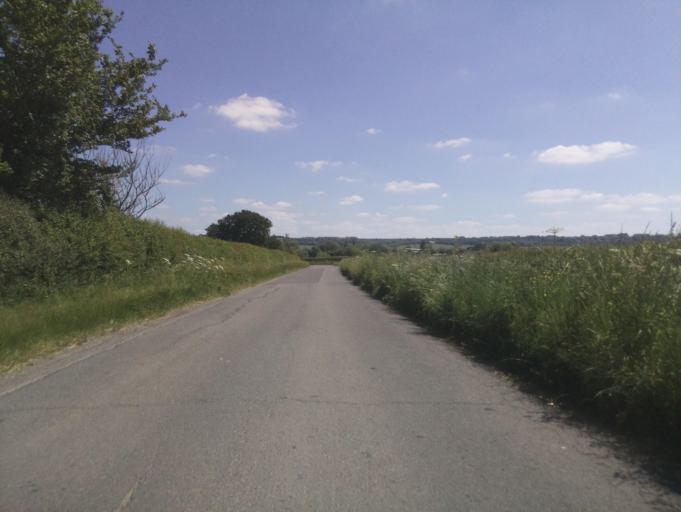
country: GB
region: England
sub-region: Wiltshire
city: Royal Wootton Bassett
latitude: 51.5149
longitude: -1.8945
